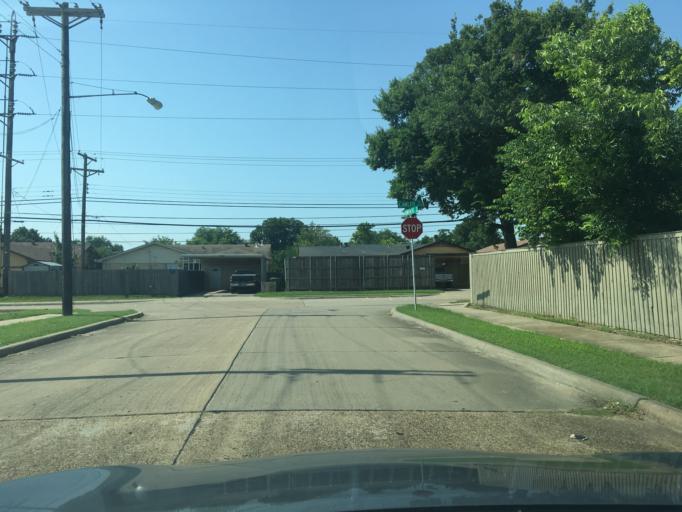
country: US
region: Texas
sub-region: Dallas County
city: Garland
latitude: 32.9242
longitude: -96.6845
